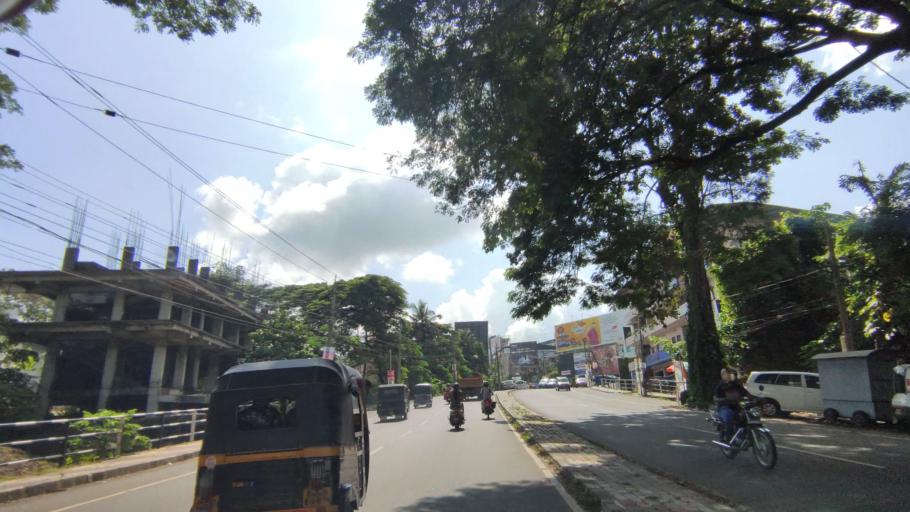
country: IN
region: Kerala
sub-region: Kottayam
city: Kottayam
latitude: 9.5918
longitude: 76.5300
